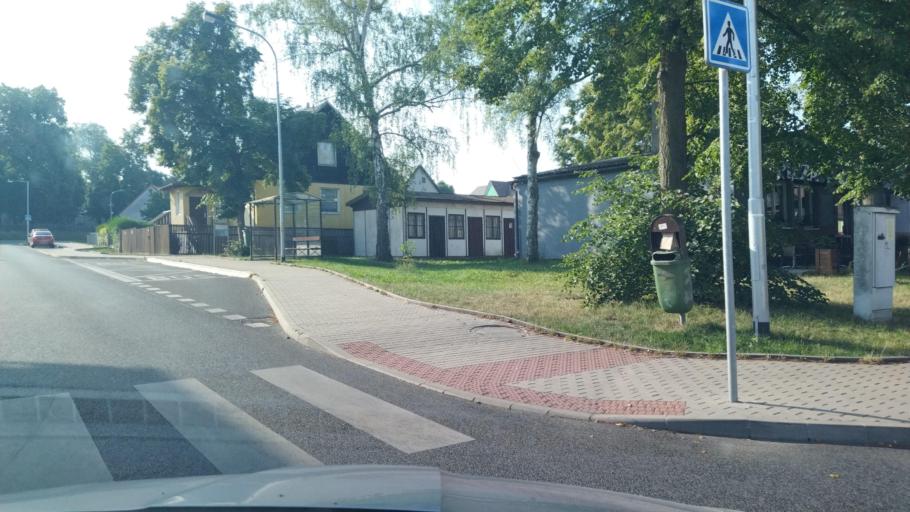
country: CZ
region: Liberecky
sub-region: Okres Ceska Lipa
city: Ceska Lipa
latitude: 50.6768
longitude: 14.5461
